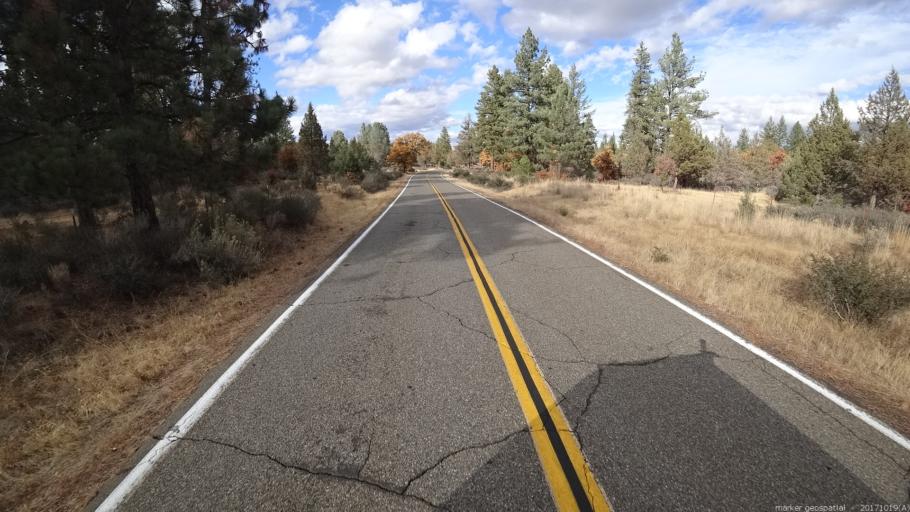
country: US
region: California
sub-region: Shasta County
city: Burney
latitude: 40.9544
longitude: -121.4406
